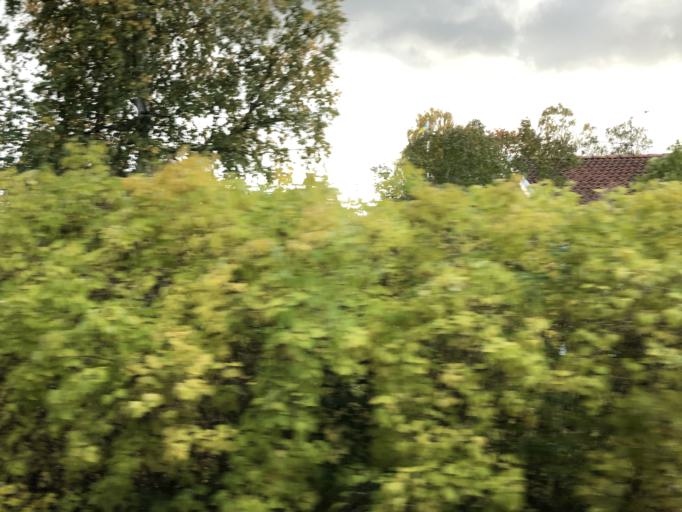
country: SE
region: Stockholm
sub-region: Jarfalla Kommun
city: Jakobsberg
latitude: 59.4284
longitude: 17.8199
